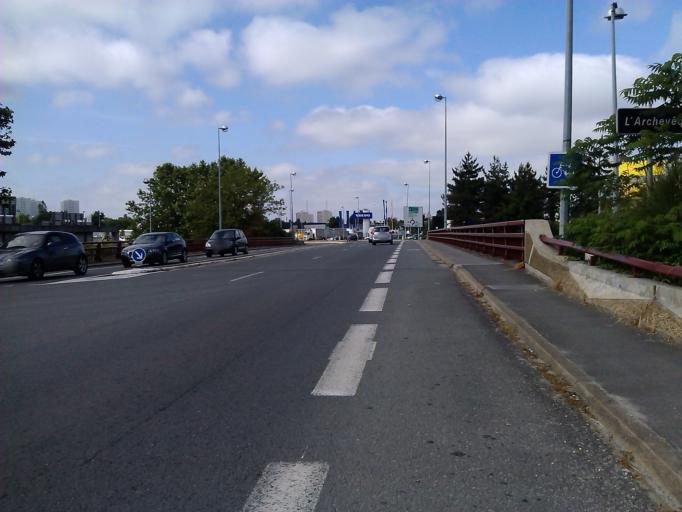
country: FR
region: Aquitaine
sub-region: Departement de la Gironde
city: Lormont
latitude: 44.8814
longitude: -0.5104
